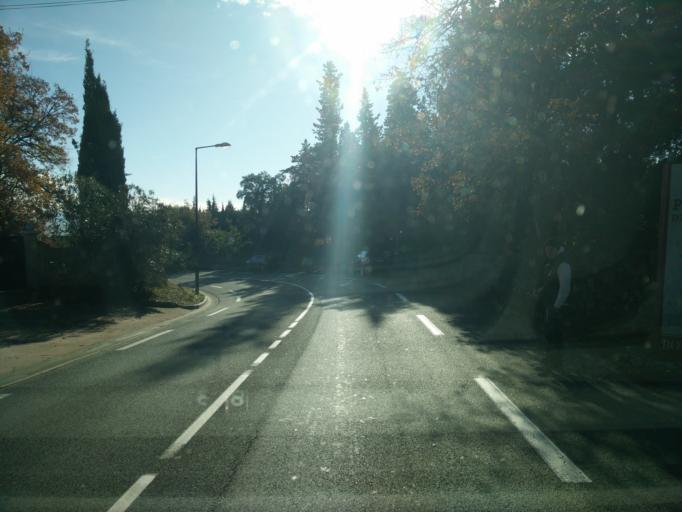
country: FR
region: Provence-Alpes-Cote d'Azur
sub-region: Departement du Var
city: Grimaud
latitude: 43.2697
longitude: 6.5280
